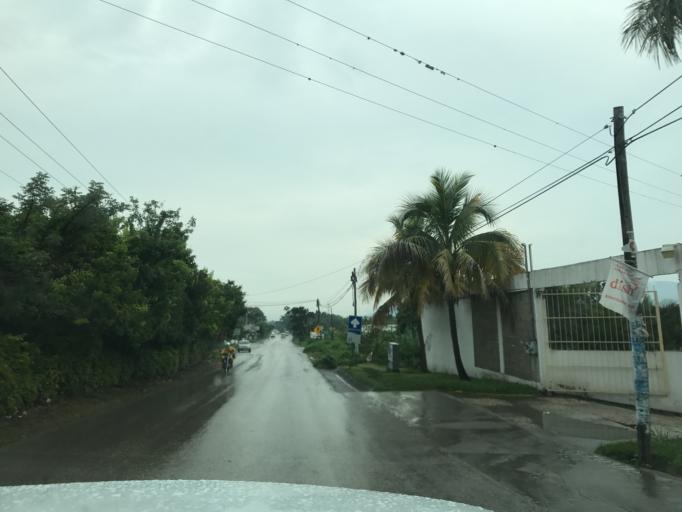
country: MX
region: Morelos
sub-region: Ayala
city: Ciudad Ayala
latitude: 18.7600
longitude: -98.9843
